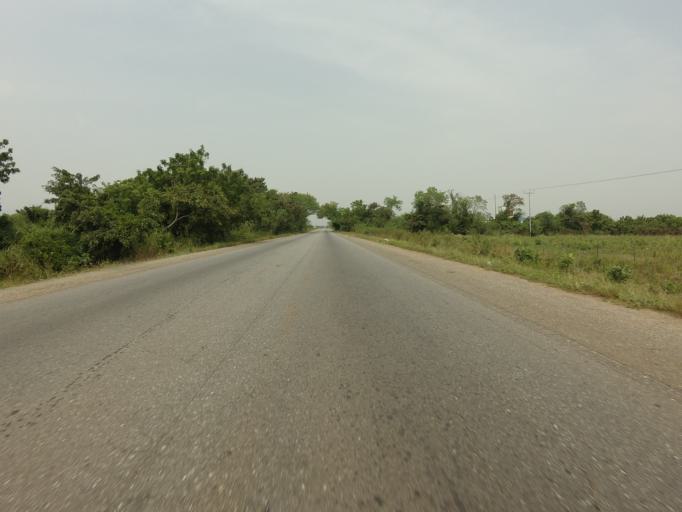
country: GH
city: Akropong
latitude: 6.0265
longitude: 0.0502
